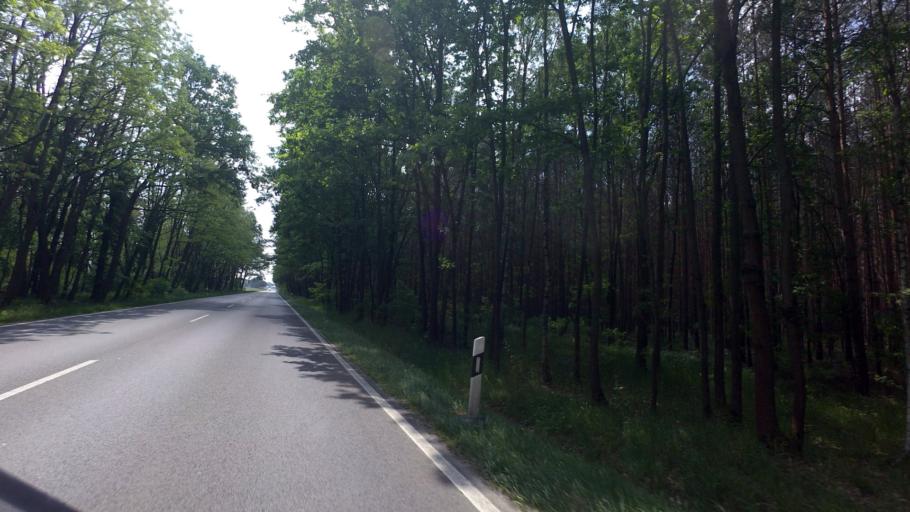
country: DE
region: Brandenburg
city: Cottbus
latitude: 51.6967
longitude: 14.3611
